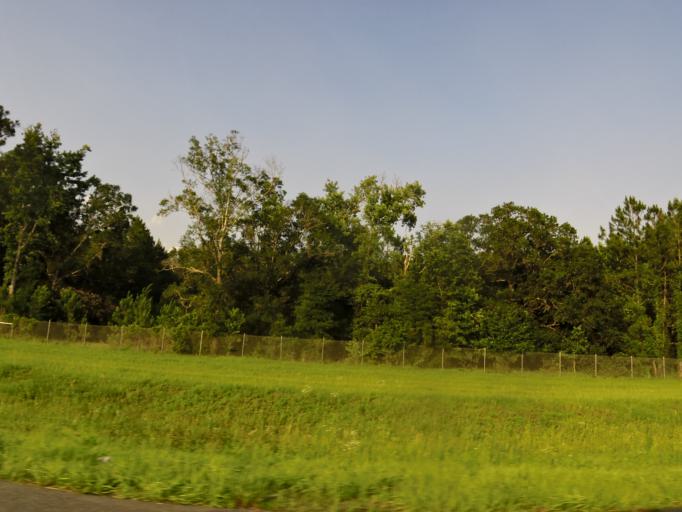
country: US
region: Florida
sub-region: Saint Johns County
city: Palm Valley
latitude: 30.1368
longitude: -81.5074
